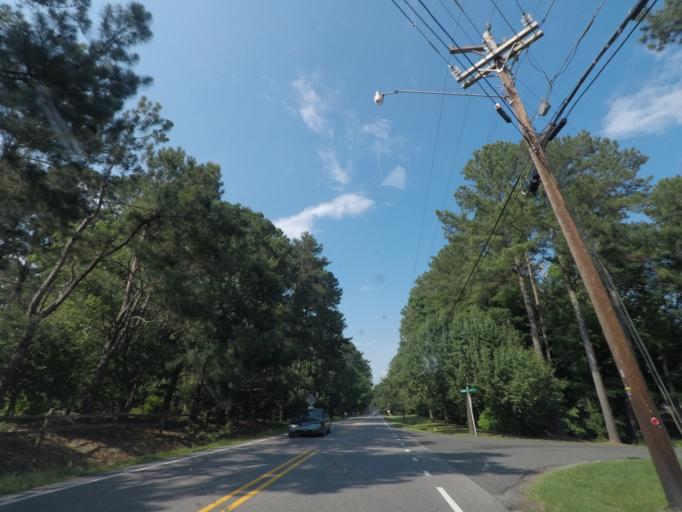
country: US
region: North Carolina
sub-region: Durham County
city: Durham
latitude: 35.9465
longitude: -78.9420
